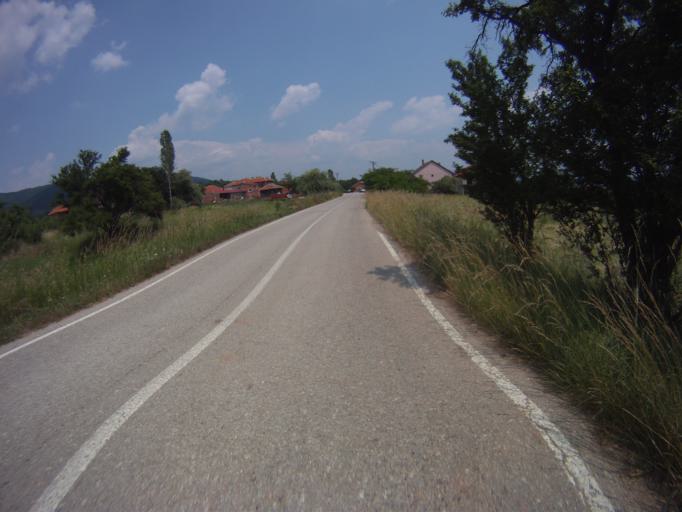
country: RS
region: Central Serbia
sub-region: Nisavski Okrug
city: Gadzin Han
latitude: 43.2034
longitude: 21.9626
